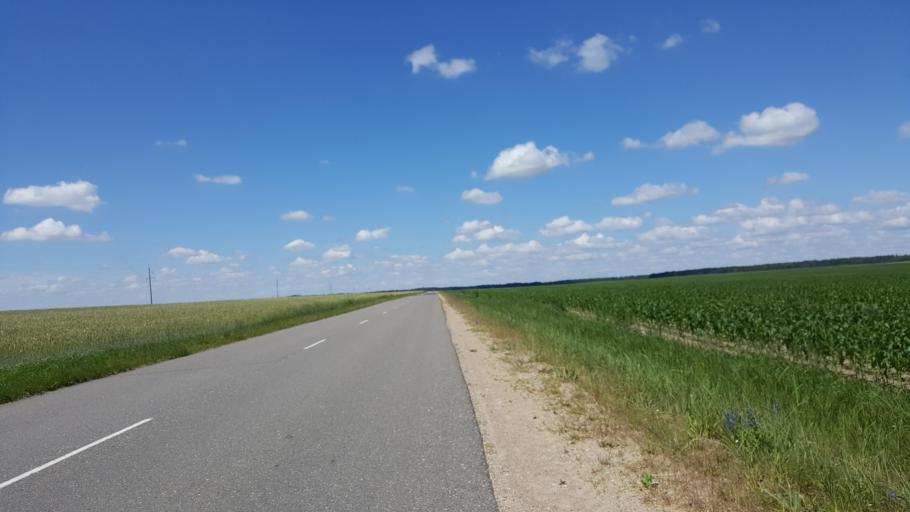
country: BY
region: Brest
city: Kamyanyets
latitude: 52.3882
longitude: 23.7340
